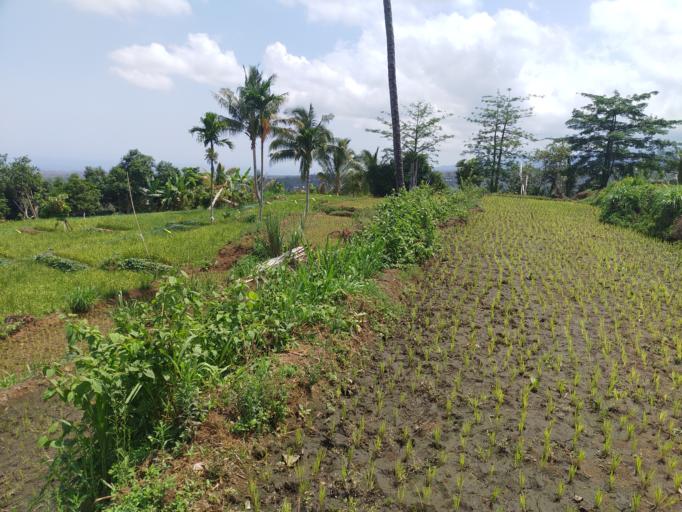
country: ID
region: West Nusa Tenggara
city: Bayan
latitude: -8.2911
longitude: 116.4035
